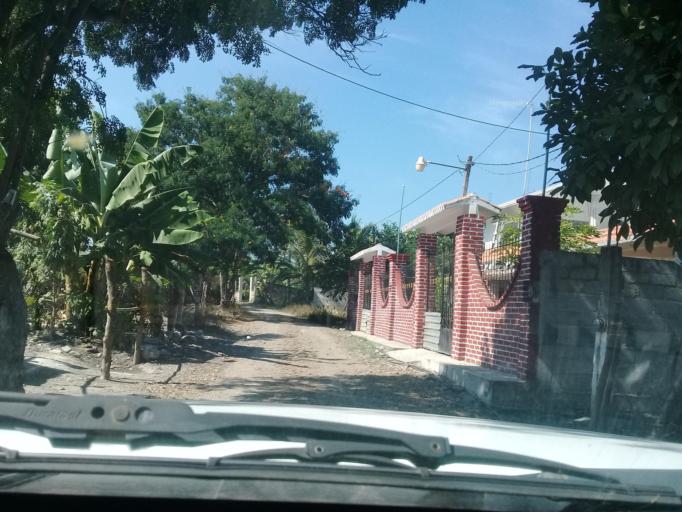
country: MX
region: Veracruz
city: Rinconada
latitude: 19.4387
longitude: -96.5637
